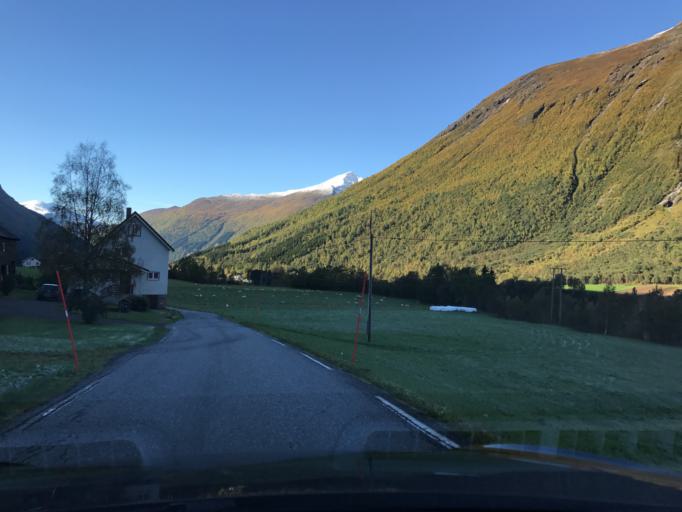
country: NO
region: More og Romsdal
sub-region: Norddal
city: Valldal
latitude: 62.3273
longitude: 7.3379
